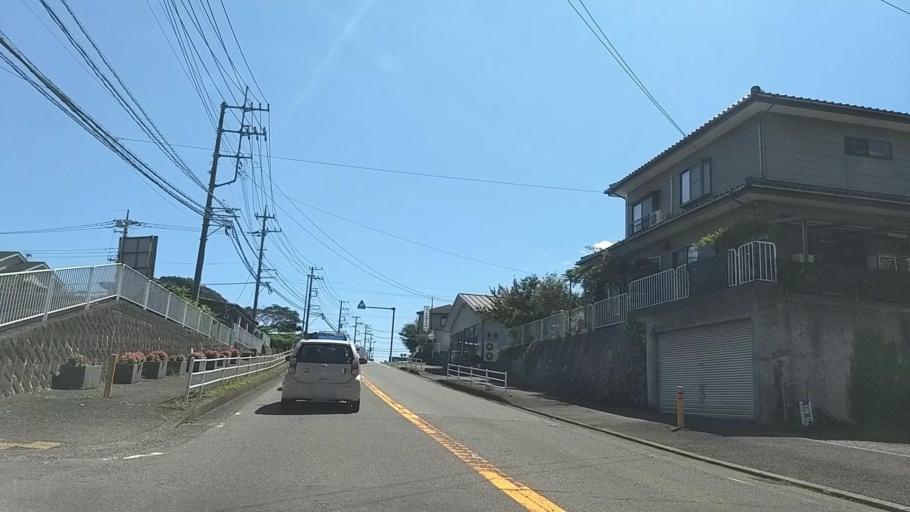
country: JP
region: Tokyo
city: Hachioji
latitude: 35.5561
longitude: 139.2613
